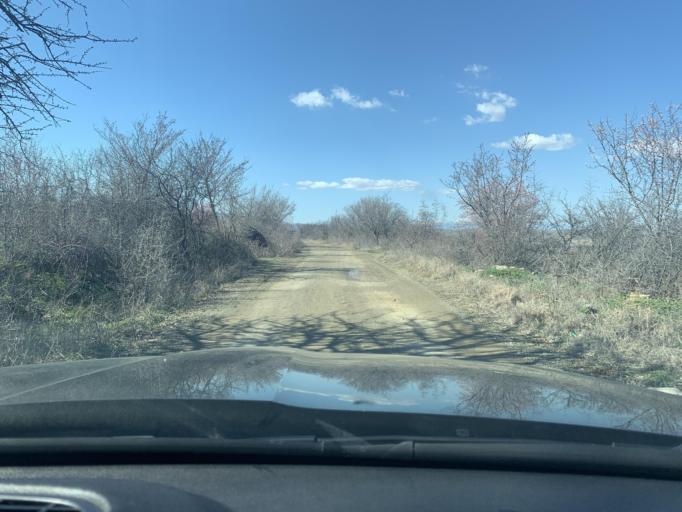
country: MK
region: Demir Kapija
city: Demir Kapija
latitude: 41.4139
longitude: 22.2205
